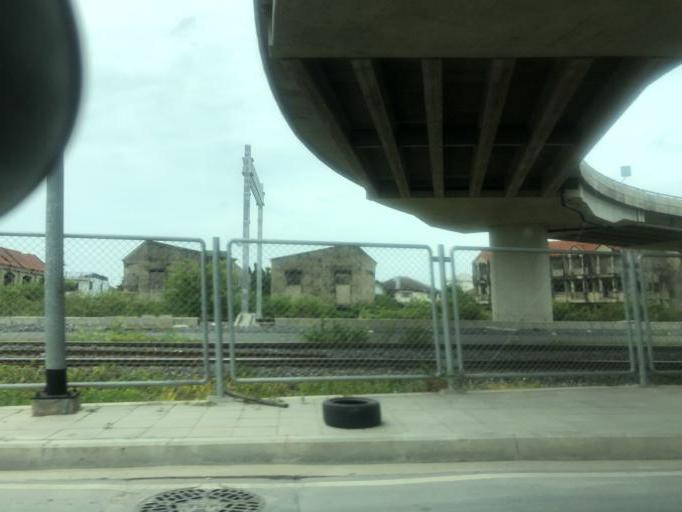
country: TH
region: Bangkok
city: Don Mueang
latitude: 13.9475
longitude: 100.6073
